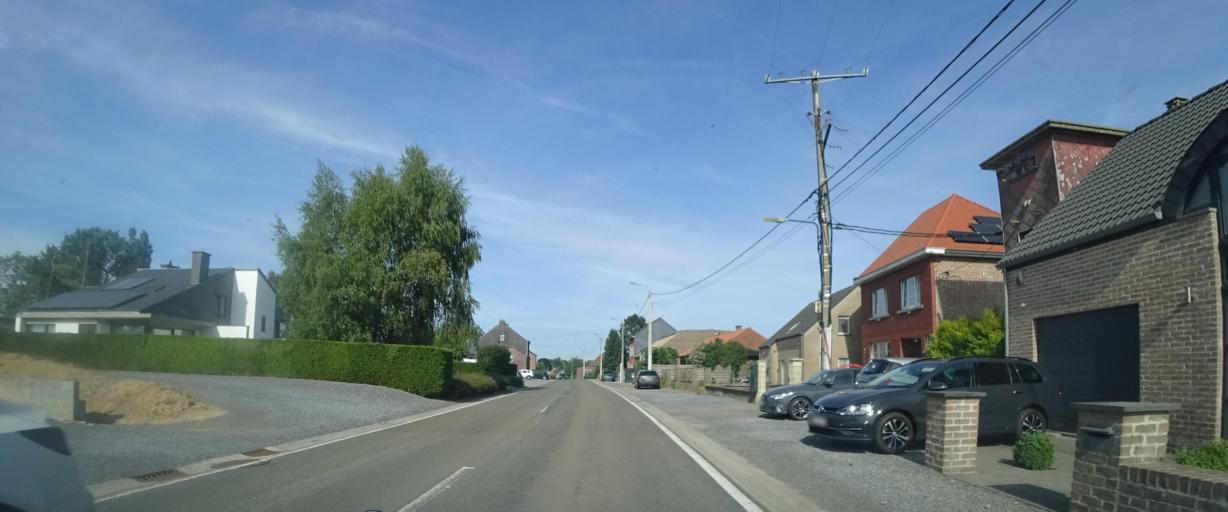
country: BE
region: Wallonia
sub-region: Province de Namur
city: Eghezee
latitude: 50.6100
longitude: 4.8972
